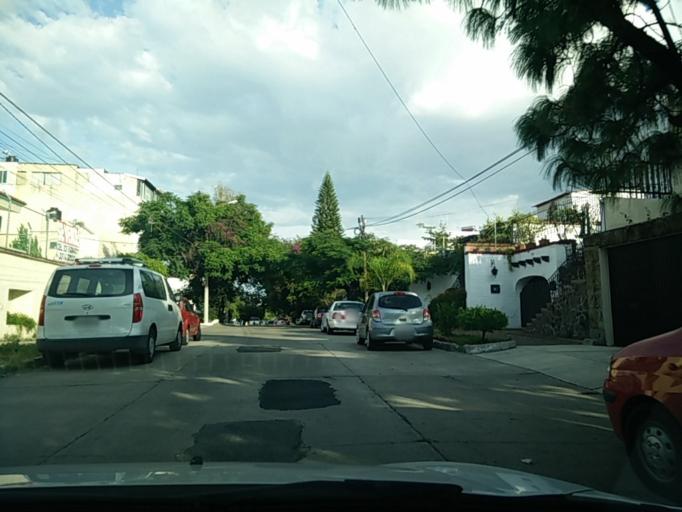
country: MX
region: Jalisco
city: Zapopan2
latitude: 20.6951
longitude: -103.3826
